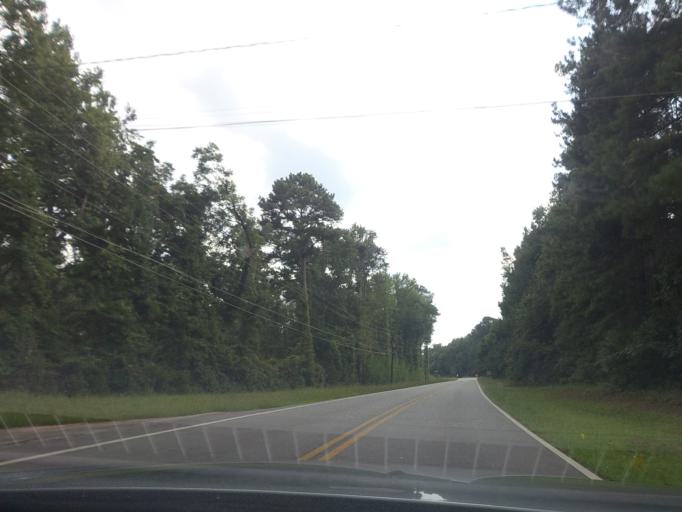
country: US
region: Georgia
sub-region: Bibb County
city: West Point
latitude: 32.8560
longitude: -83.7842
